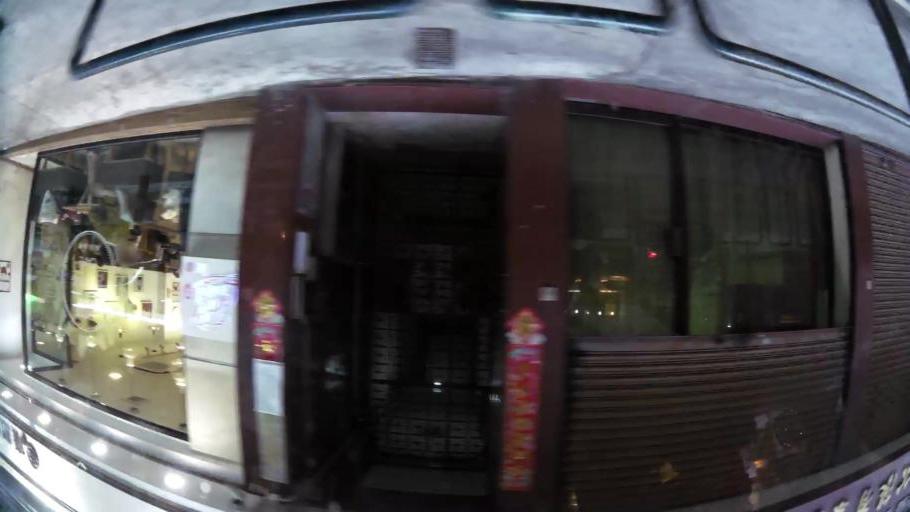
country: MO
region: Macau
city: Macau
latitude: 22.2012
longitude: 113.5430
